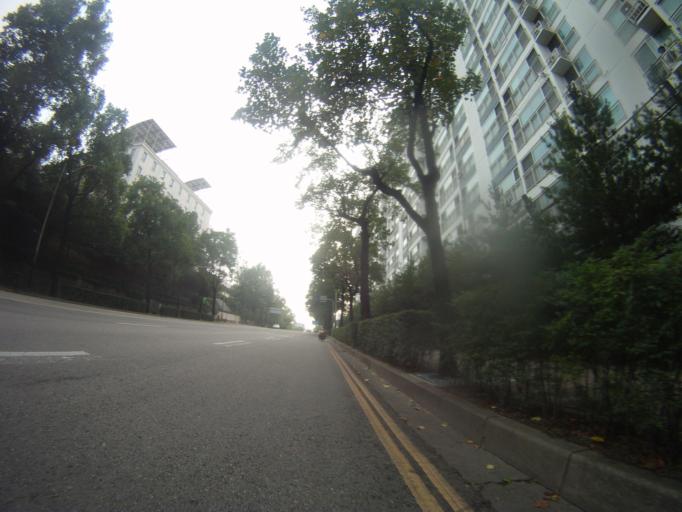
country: KR
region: Incheon
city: Incheon
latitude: 37.4569
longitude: 126.6999
